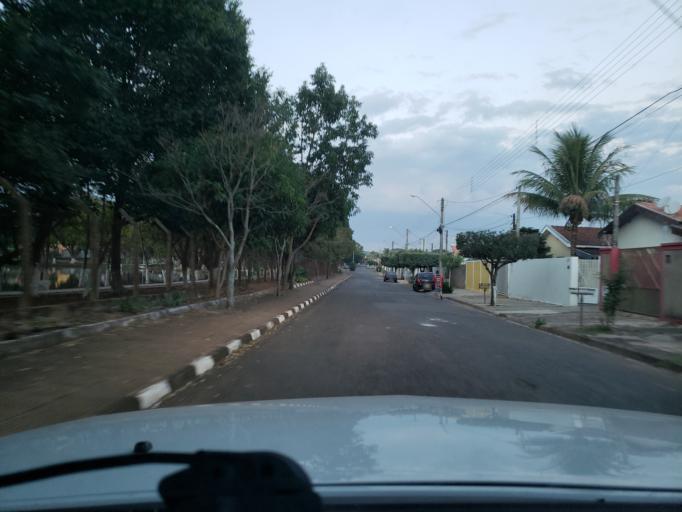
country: BR
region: Sao Paulo
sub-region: Moji-Guacu
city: Mogi-Gaucu
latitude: -22.3423
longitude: -46.9337
